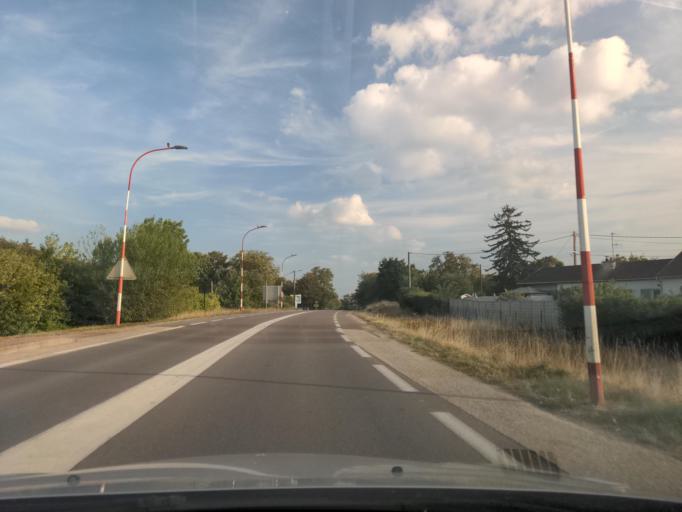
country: FR
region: Bourgogne
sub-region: Departement de la Cote-d'Or
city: Sennecey-les-Dijon
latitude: 47.2879
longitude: 5.0983
